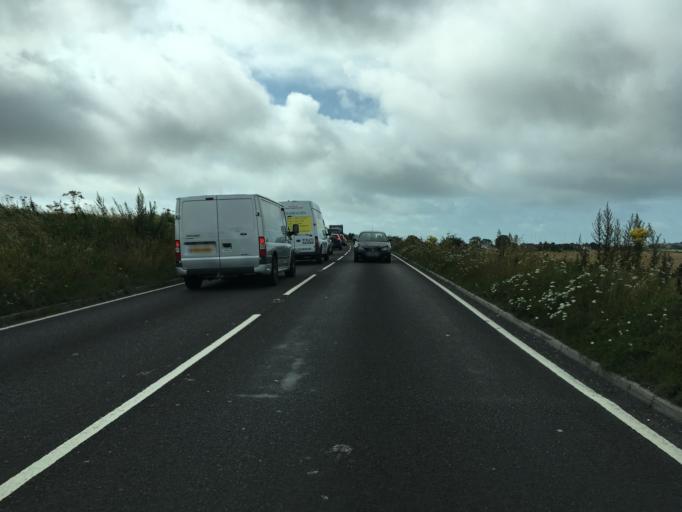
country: GB
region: England
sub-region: Brighton and Hove
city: Rottingdean
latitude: 50.8423
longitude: -0.0742
